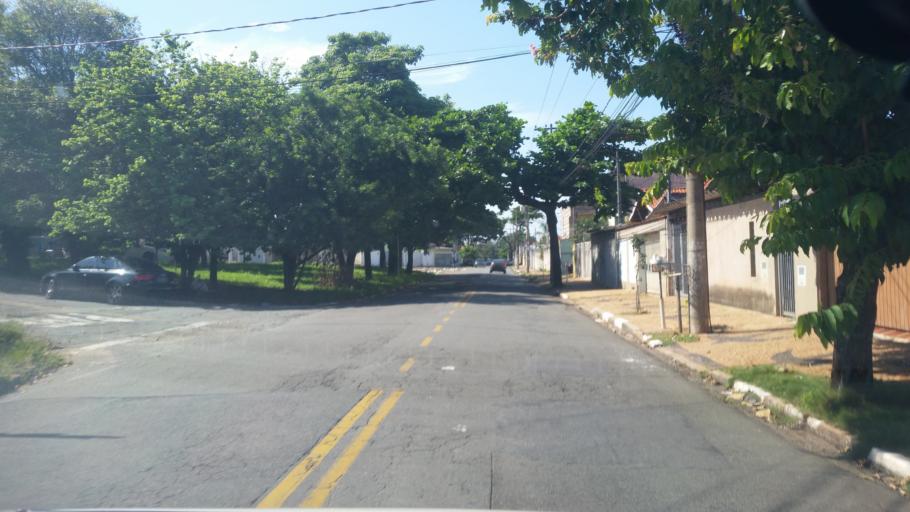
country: BR
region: Sao Paulo
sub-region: Campinas
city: Campinas
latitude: -22.8636
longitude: -47.0665
